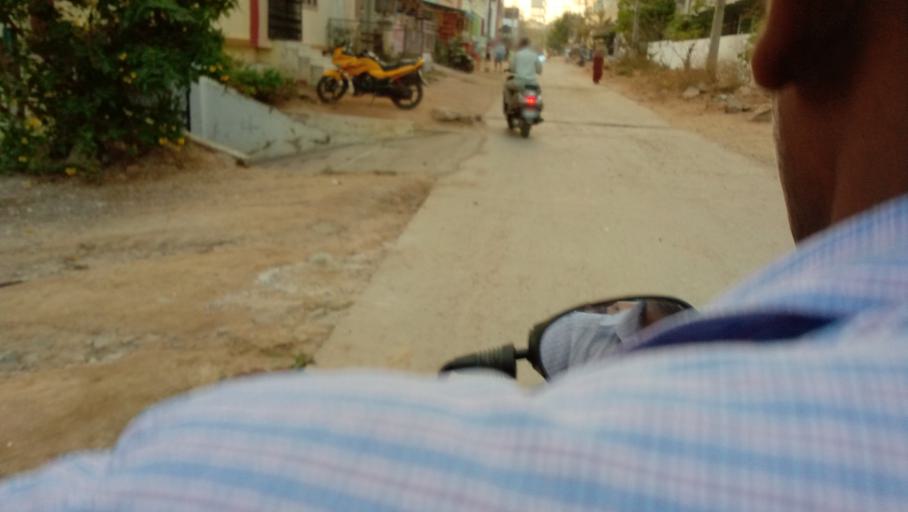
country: IN
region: Telangana
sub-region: Medak
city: Serilingampalle
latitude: 17.5182
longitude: 78.3106
